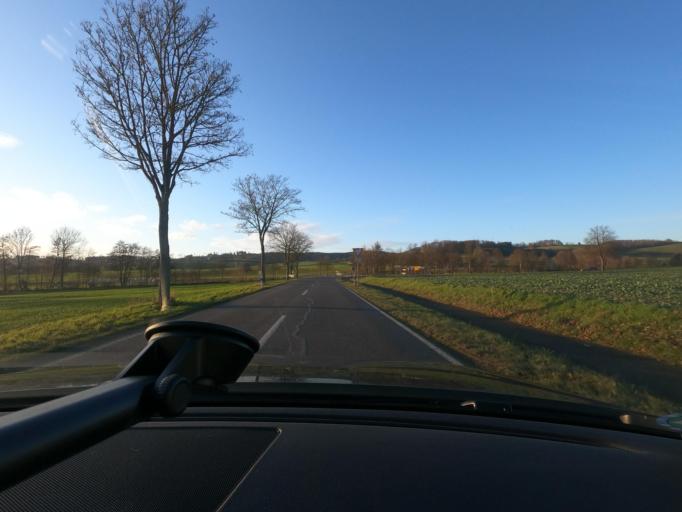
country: DE
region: Lower Saxony
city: Eisdorf am Harz
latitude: 51.7698
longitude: 10.1862
